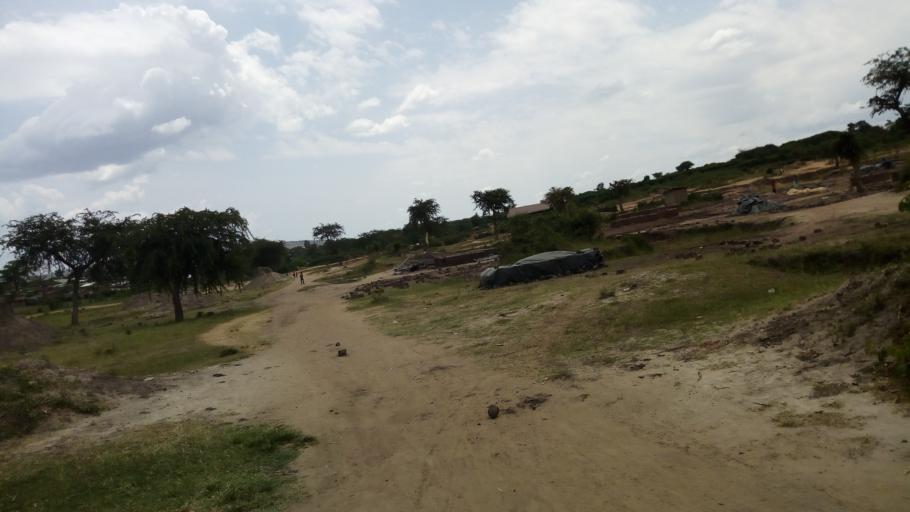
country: UG
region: Western Region
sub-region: Isingiro District
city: Isingiro
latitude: -0.7720
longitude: 30.9450
